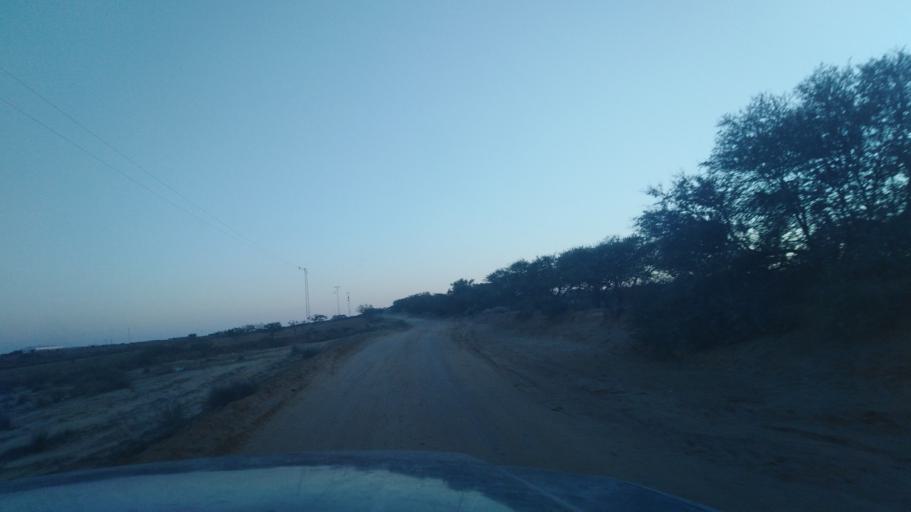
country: TN
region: Safaqis
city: Sfax
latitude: 34.7336
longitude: 10.4449
